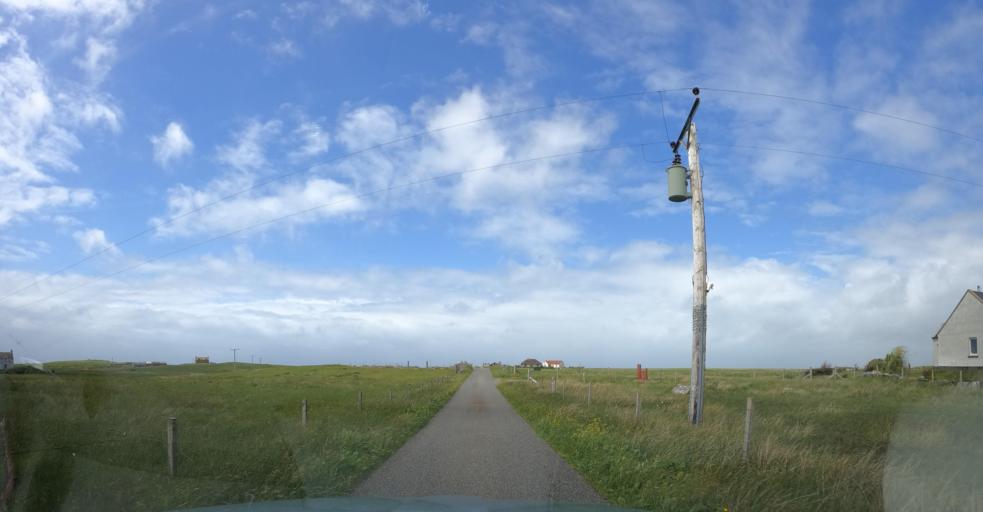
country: GB
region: Scotland
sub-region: Eilean Siar
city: Isle of South Uist
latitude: 57.2764
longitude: -7.4106
